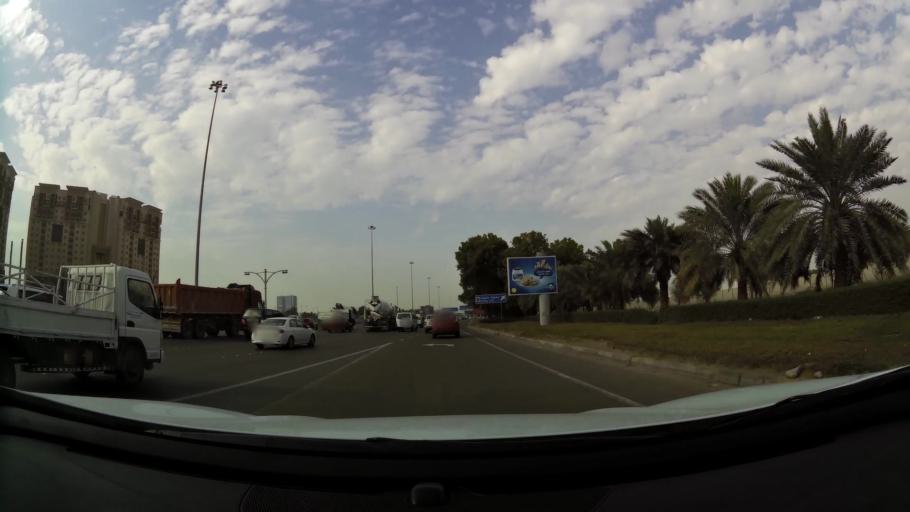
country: AE
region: Abu Dhabi
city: Abu Dhabi
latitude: 24.3835
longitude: 54.5247
